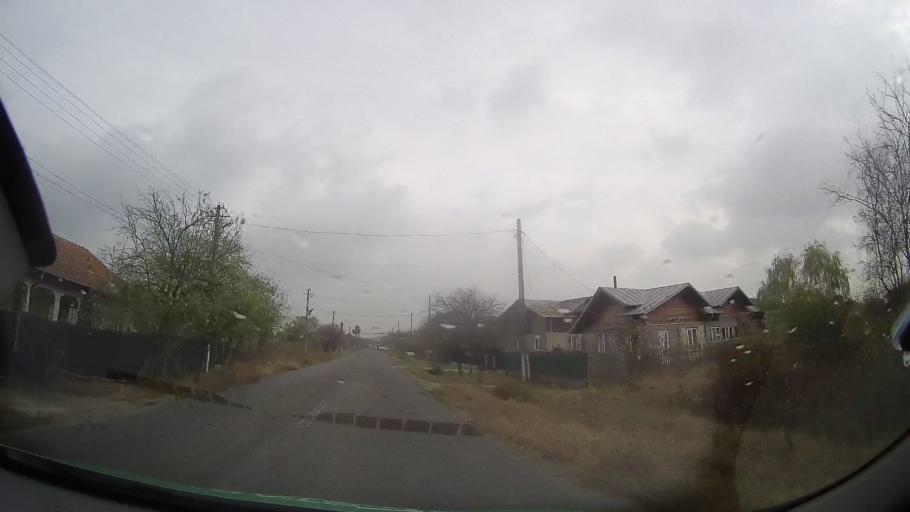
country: RO
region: Prahova
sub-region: Comuna Draganesti
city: Draganesti
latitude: 44.8294
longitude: 26.2781
